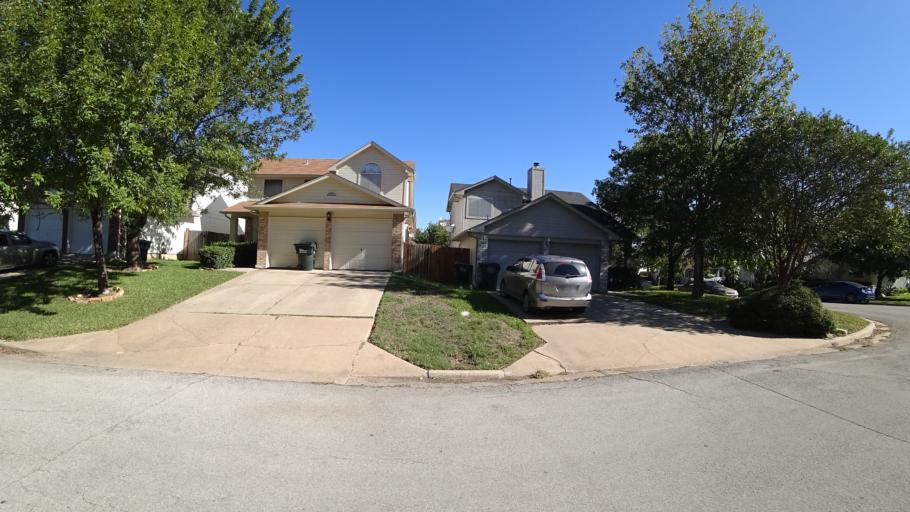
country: US
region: Texas
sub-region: Travis County
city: Manor
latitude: 30.3325
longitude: -97.6457
